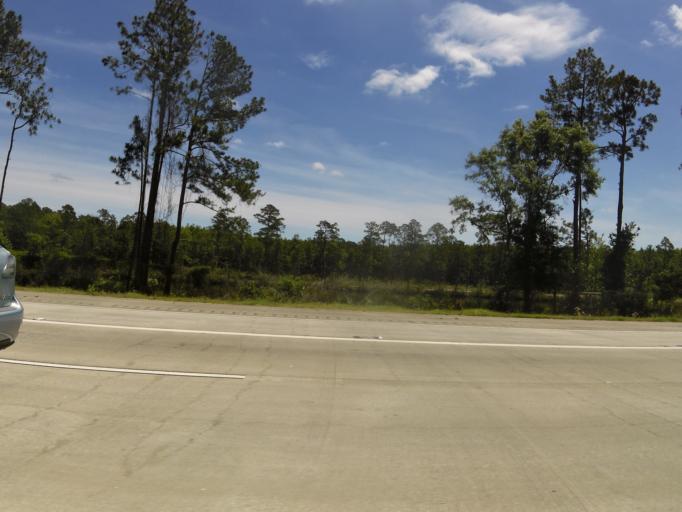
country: US
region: Georgia
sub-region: McIntosh County
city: Darien
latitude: 31.2990
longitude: -81.4821
